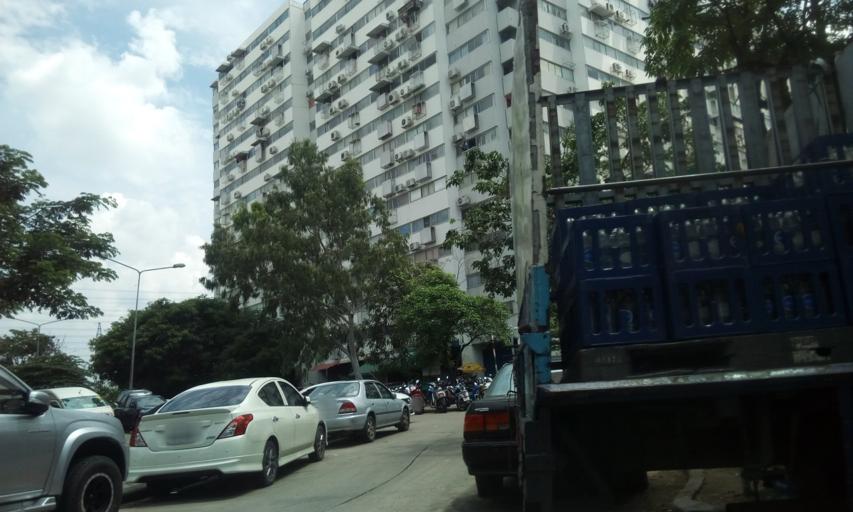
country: TH
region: Bangkok
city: Lak Si
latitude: 13.9090
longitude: 100.5535
